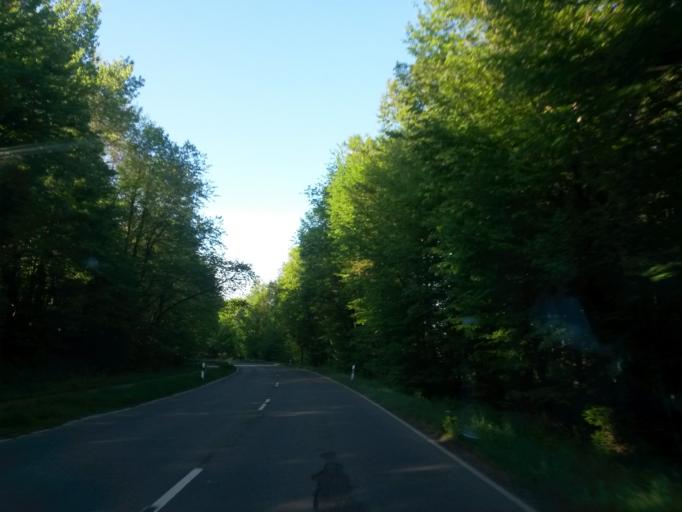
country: DE
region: North Rhine-Westphalia
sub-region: Regierungsbezirk Koln
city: Ruppichteroth
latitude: 50.9097
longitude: 7.4806
